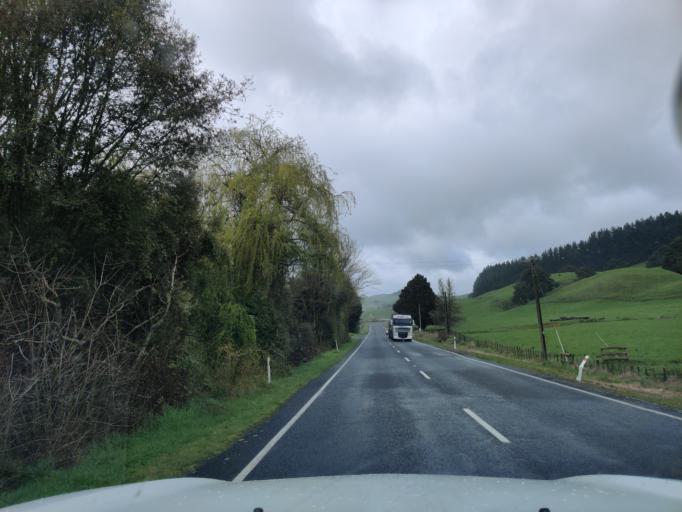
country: NZ
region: Waikato
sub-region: Otorohanga District
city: Otorohanga
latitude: -38.6889
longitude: 175.2111
